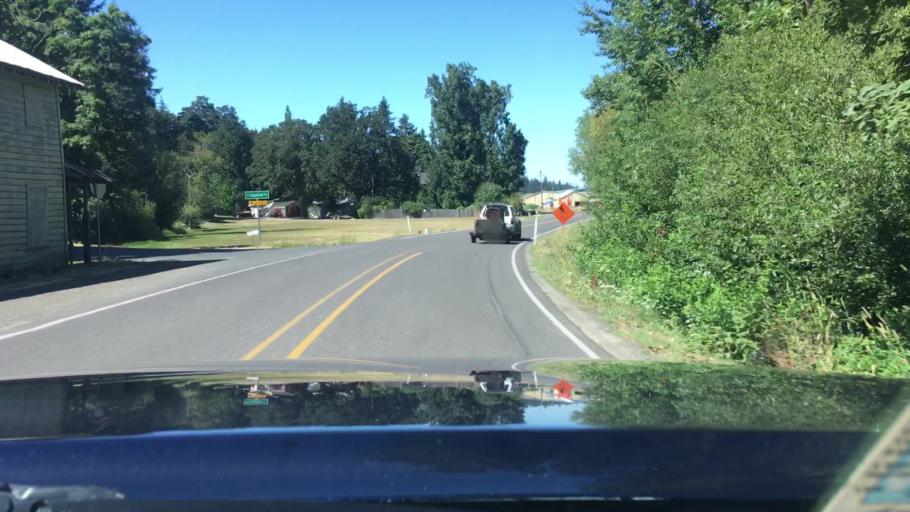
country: US
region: Oregon
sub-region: Lane County
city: Cottage Grove
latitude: 43.8300
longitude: -123.0451
